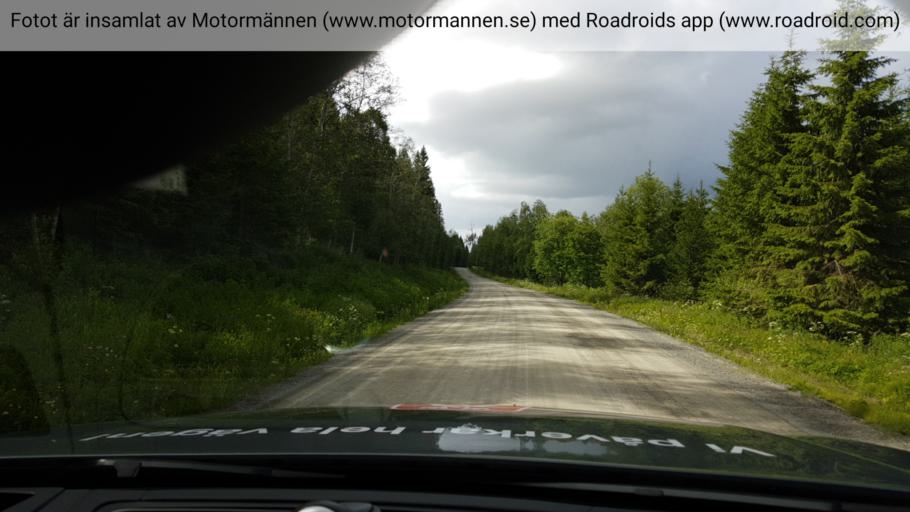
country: SE
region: Jaemtland
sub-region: Bergs Kommun
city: Hoverberg
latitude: 62.9273
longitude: 14.2959
